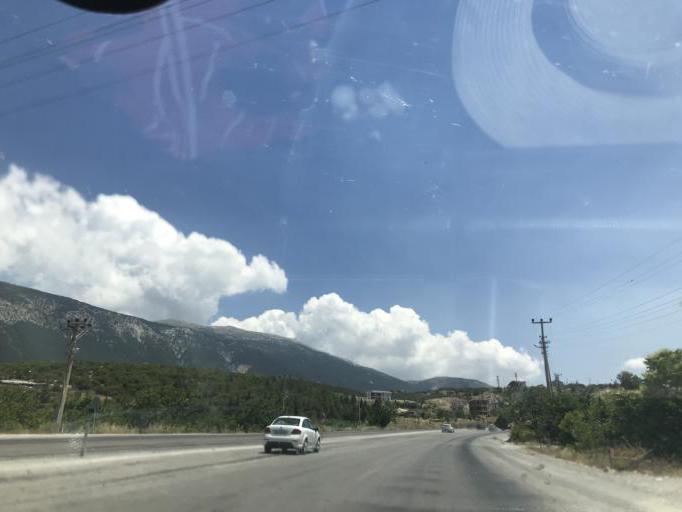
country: TR
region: Denizli
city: Honaz
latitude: 37.6926
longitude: 29.2136
